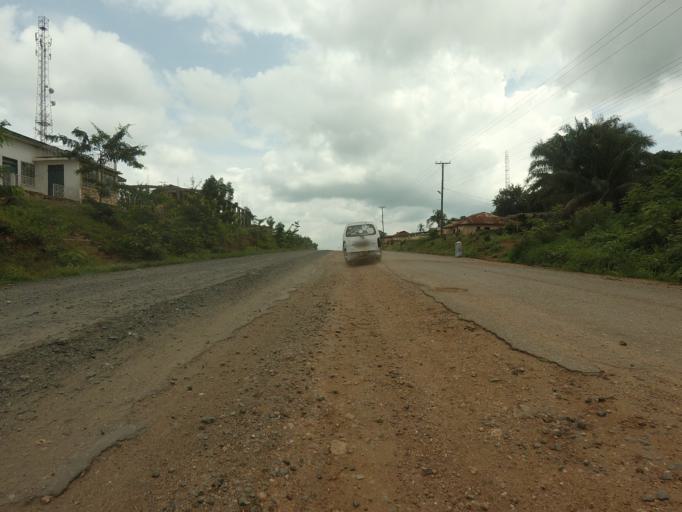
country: GH
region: Volta
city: Ho
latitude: 6.6248
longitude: 0.3101
